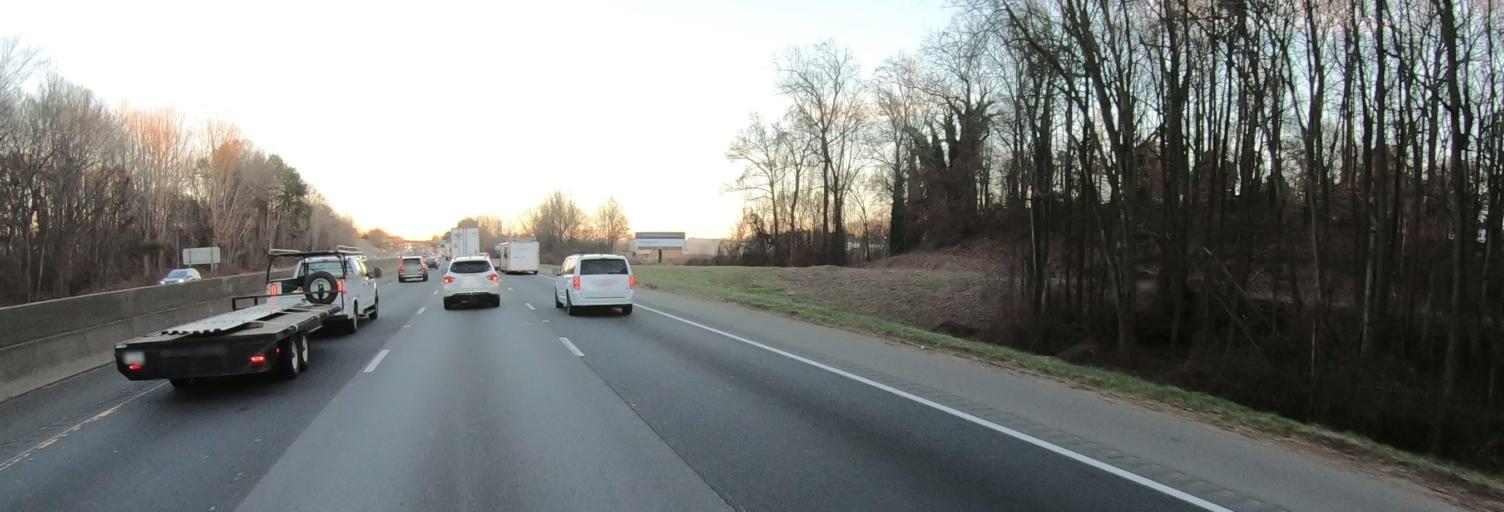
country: US
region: North Carolina
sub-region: Gaston County
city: Ranlo
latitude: 35.2678
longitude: -81.1411
